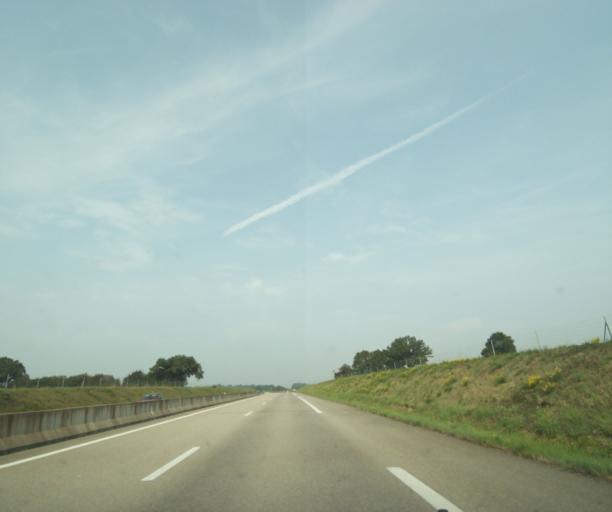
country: FR
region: Lower Normandy
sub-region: Departement de l'Orne
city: Ecouche
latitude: 48.7772
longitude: -0.1144
